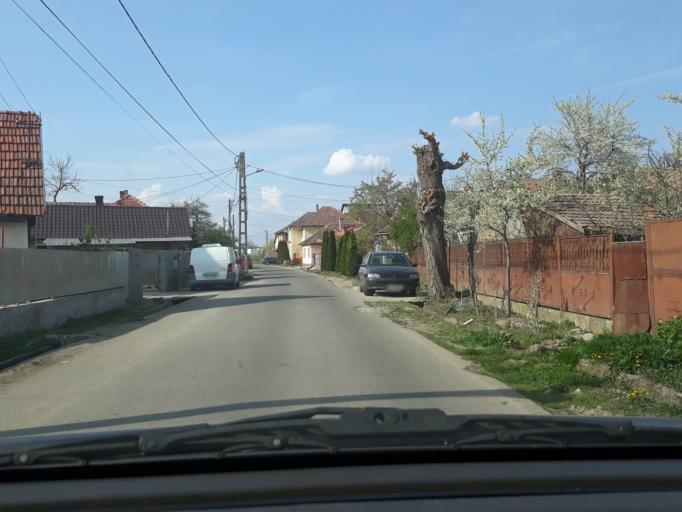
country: RO
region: Bihor
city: Margita
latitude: 47.3478
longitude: 22.3288
